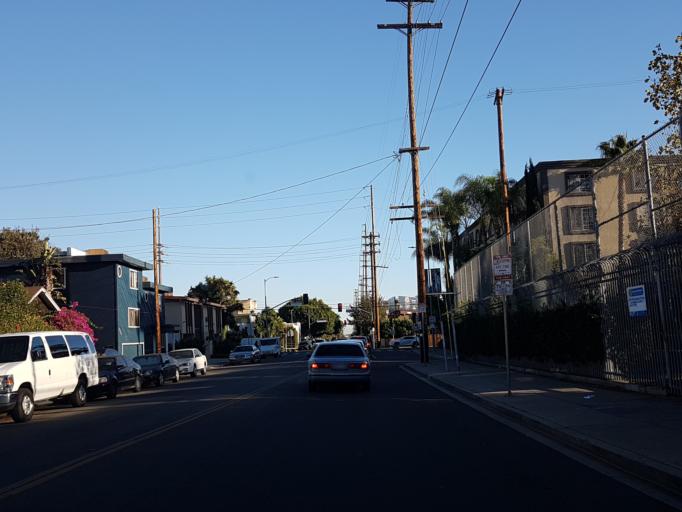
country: US
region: California
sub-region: Los Angeles County
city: Westwood, Los Angeles
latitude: 34.0452
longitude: -118.4573
